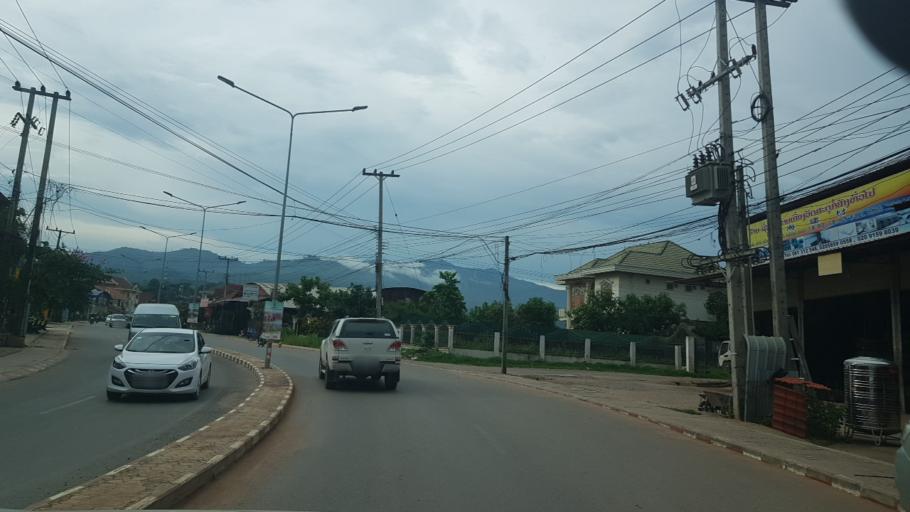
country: LA
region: Oudomxai
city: Muang Xay
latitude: 20.6782
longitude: 101.9869
